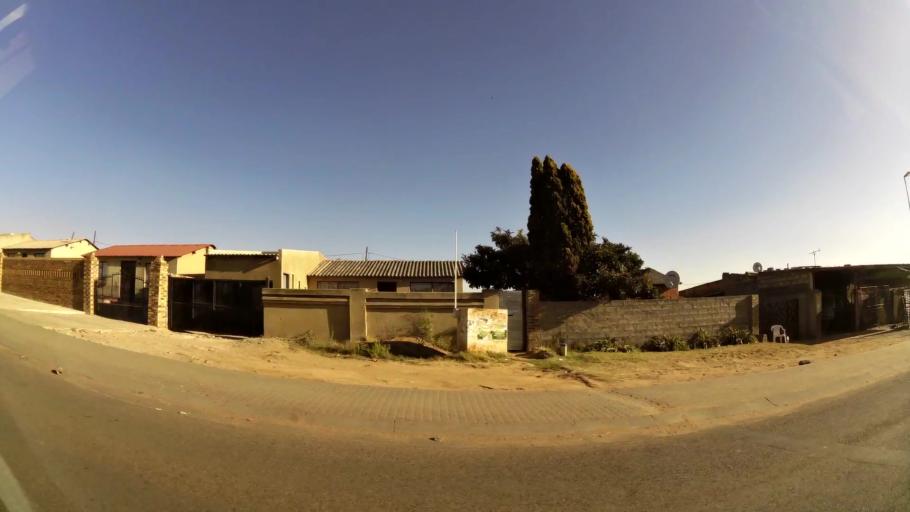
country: ZA
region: Gauteng
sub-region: Ekurhuleni Metropolitan Municipality
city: Tembisa
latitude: -26.0128
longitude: 28.2243
